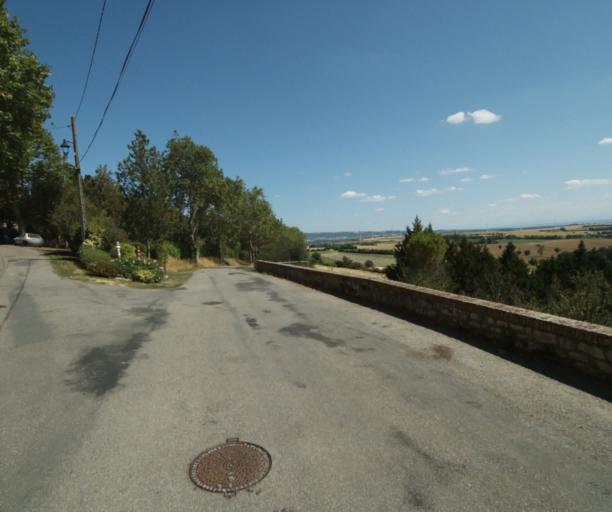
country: FR
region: Midi-Pyrenees
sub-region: Departement de la Haute-Garonne
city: Saint-Felix-Lauragais
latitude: 43.4891
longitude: 1.8978
